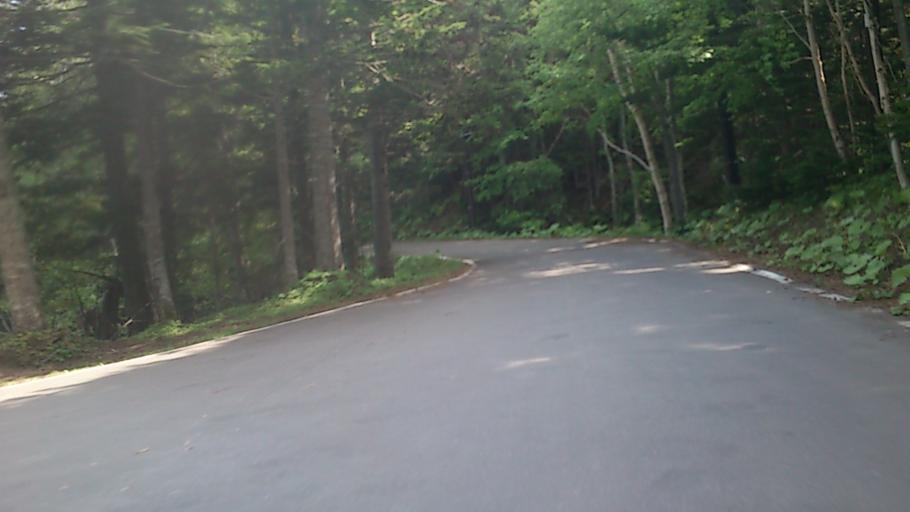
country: JP
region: Hokkaido
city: Kitami
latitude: 43.3850
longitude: 143.9661
